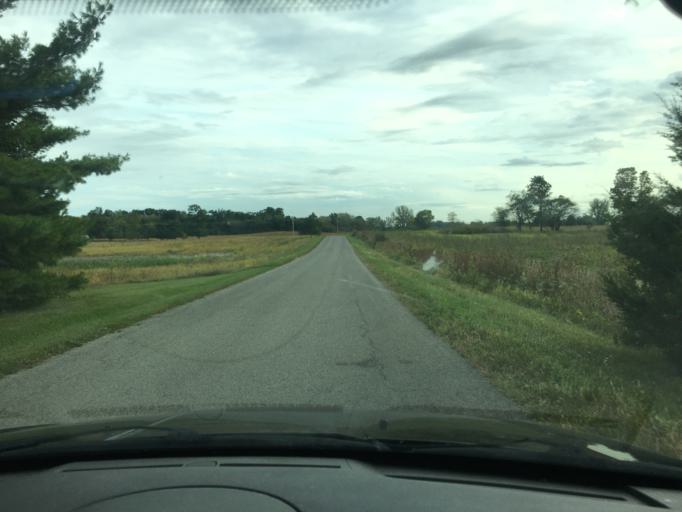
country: US
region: Ohio
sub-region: Logan County
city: Bellefontaine
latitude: 40.3115
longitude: -83.8071
